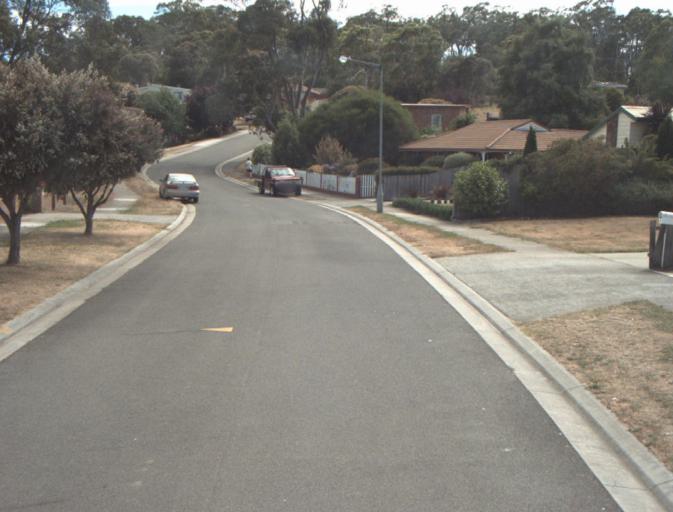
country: AU
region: Tasmania
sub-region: Launceston
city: West Launceston
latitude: -41.4576
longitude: 147.1240
